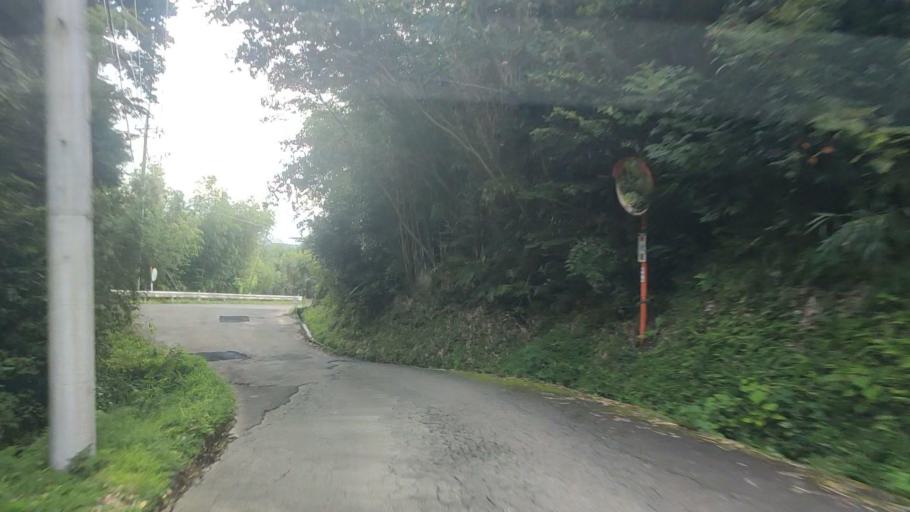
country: JP
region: Shizuoka
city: Mishima
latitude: 35.1195
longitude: 138.9784
